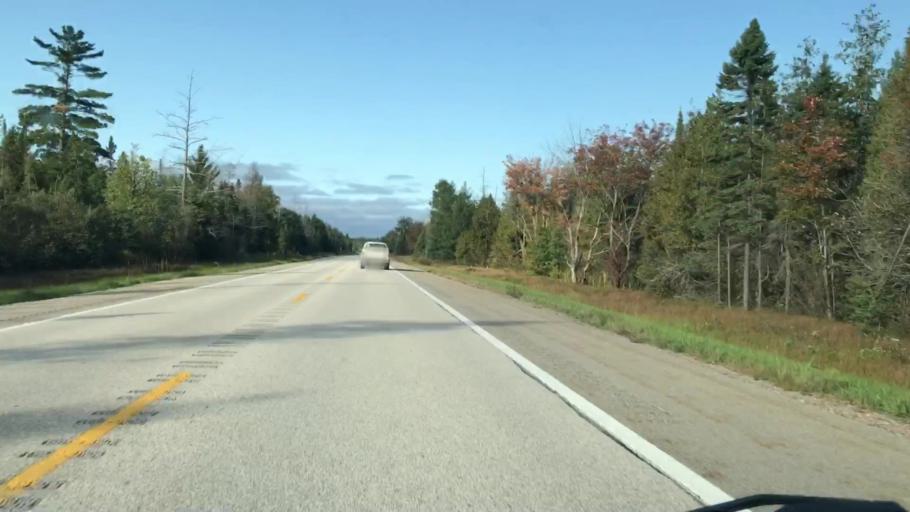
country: US
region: Michigan
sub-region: Luce County
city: Newberry
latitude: 46.3219
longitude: -85.1810
